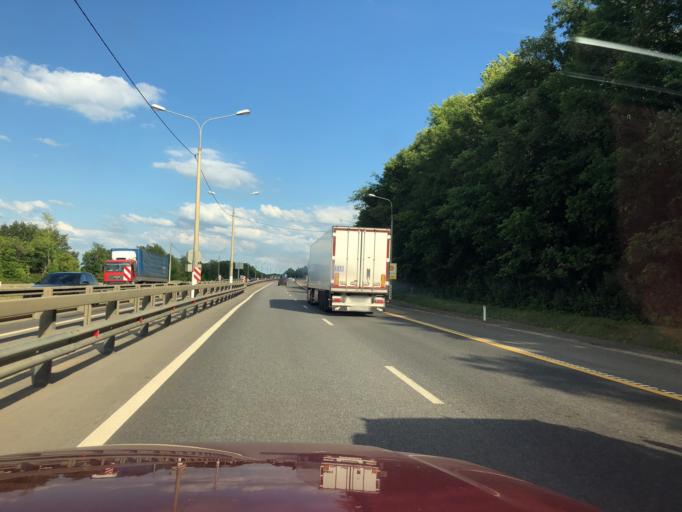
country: RU
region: Lipetsk
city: Zadonsk
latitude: 52.4406
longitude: 38.8021
